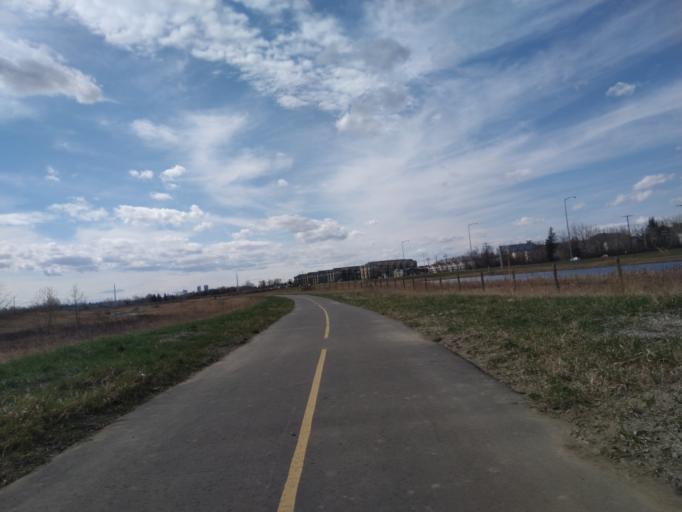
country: CA
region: Alberta
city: Chestermere
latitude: 51.0363
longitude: -113.9253
